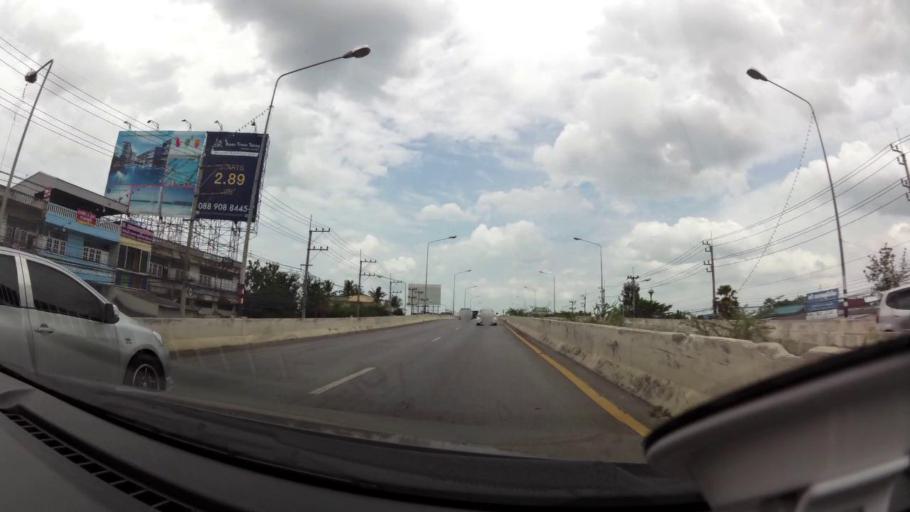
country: TH
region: Phetchaburi
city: Cha-am
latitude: 12.8052
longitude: 99.9654
